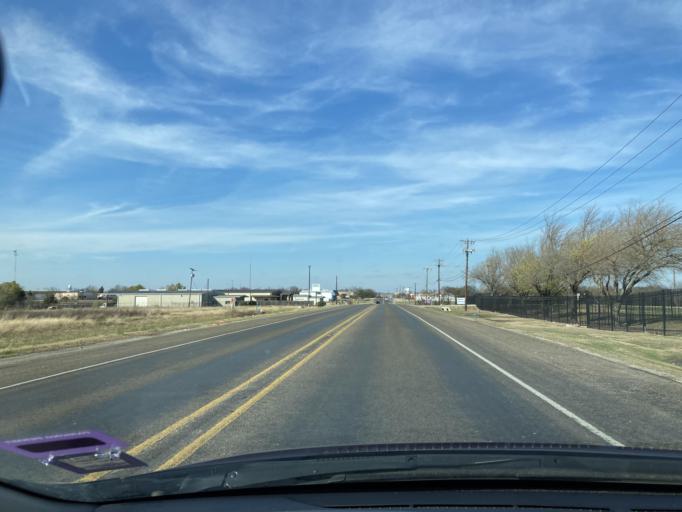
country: US
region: Texas
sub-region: Navarro County
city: Corsicana
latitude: 32.0773
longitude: -96.4475
